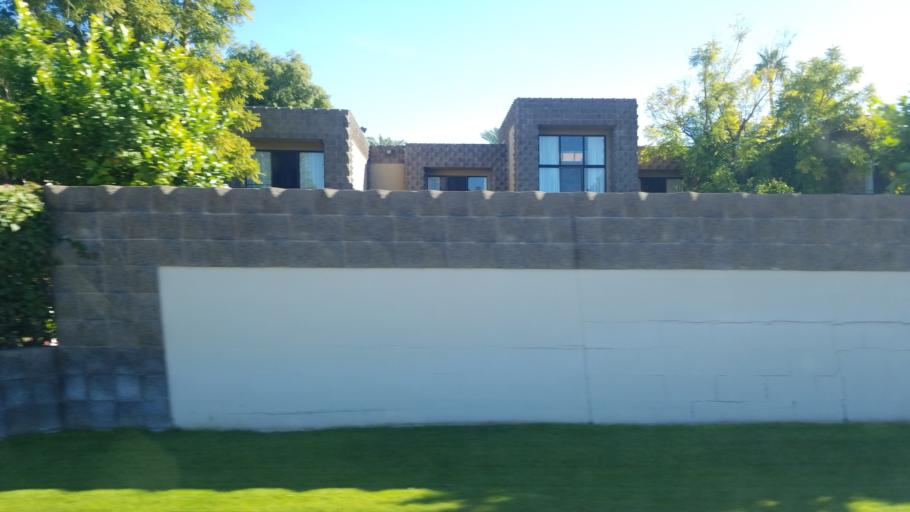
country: US
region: Arizona
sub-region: Maricopa County
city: Paradise Valley
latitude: 33.5142
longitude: -111.9258
